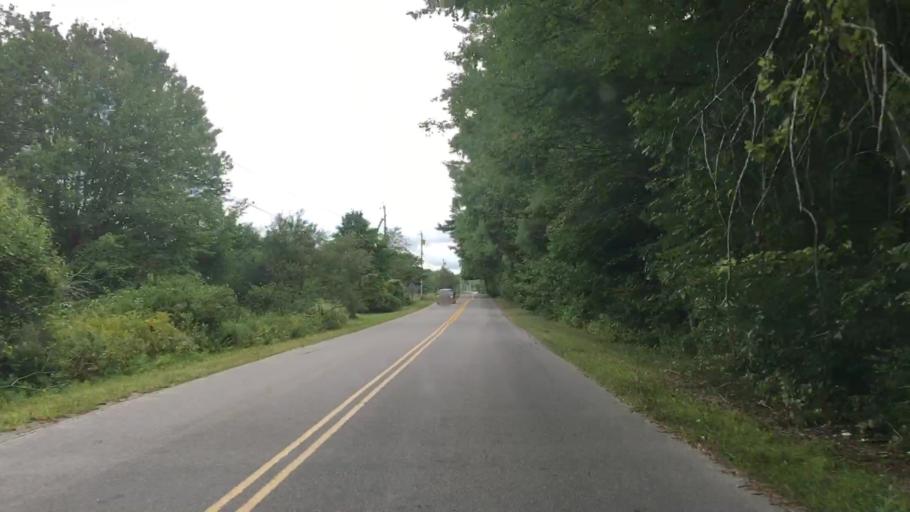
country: US
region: Maine
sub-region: Kennebec County
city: Hallowell
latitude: 44.2749
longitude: -69.8112
